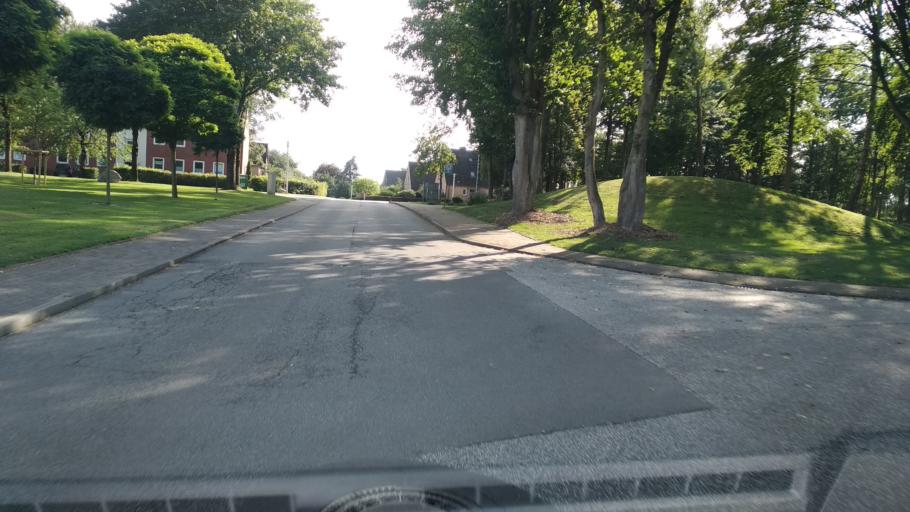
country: DE
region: Schleswig-Holstein
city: Busdorf
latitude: 54.4882
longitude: 9.5466
